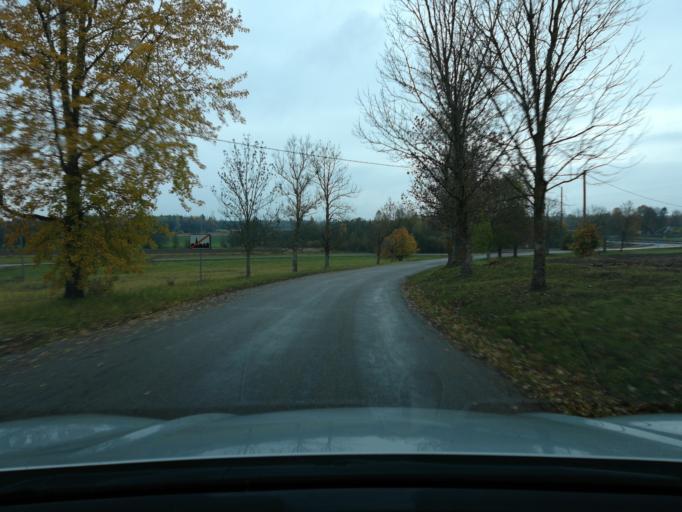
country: EE
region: Ida-Virumaa
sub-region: Johvi vald
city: Johvi
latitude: 59.2029
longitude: 27.5341
